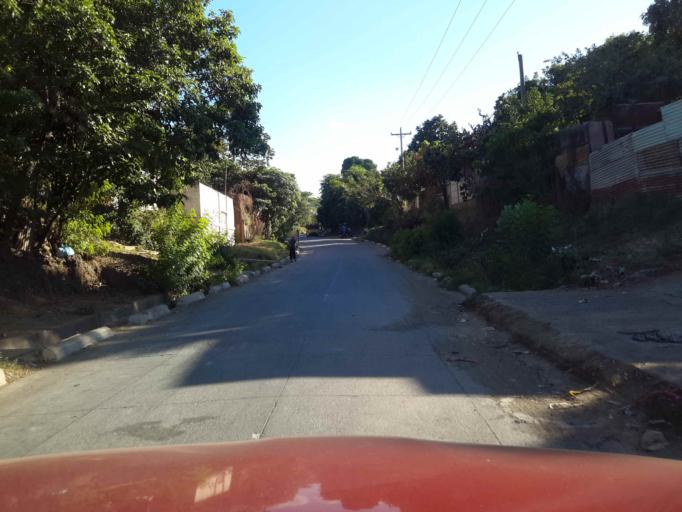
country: NI
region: Managua
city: Managua
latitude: 12.1117
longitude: -86.2912
